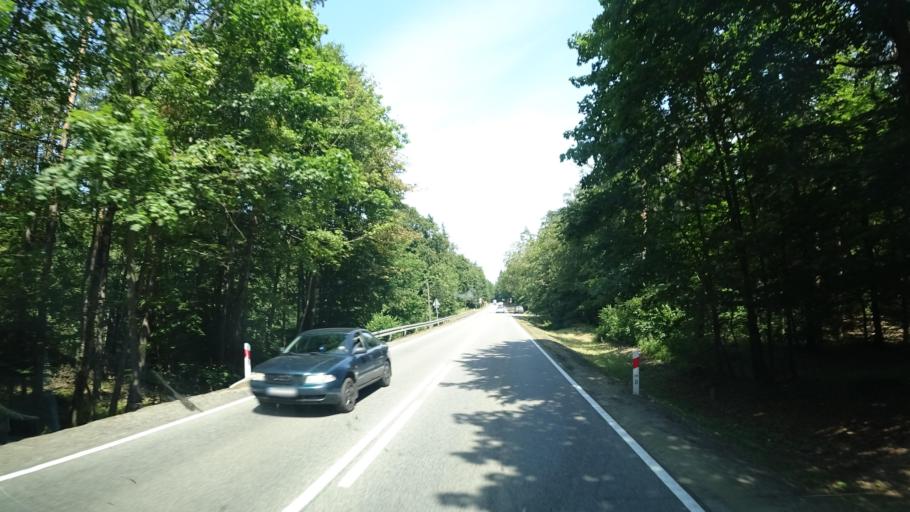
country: PL
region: Pomeranian Voivodeship
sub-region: Powiat koscierski
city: Grabowo Koscierskie
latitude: 54.2137
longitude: 18.1164
